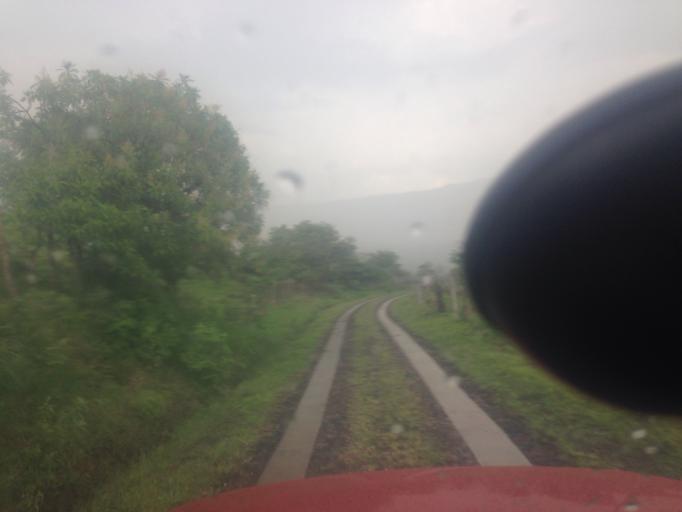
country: MX
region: Nayarit
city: Jala
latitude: 21.1120
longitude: -104.4790
